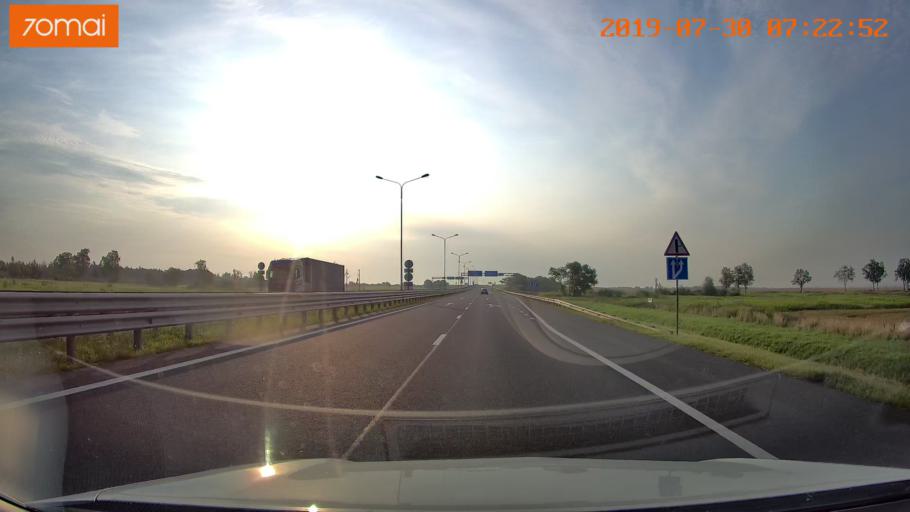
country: RU
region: Kaliningrad
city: Bol'shoe Isakovo
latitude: 54.6920
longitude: 20.7680
